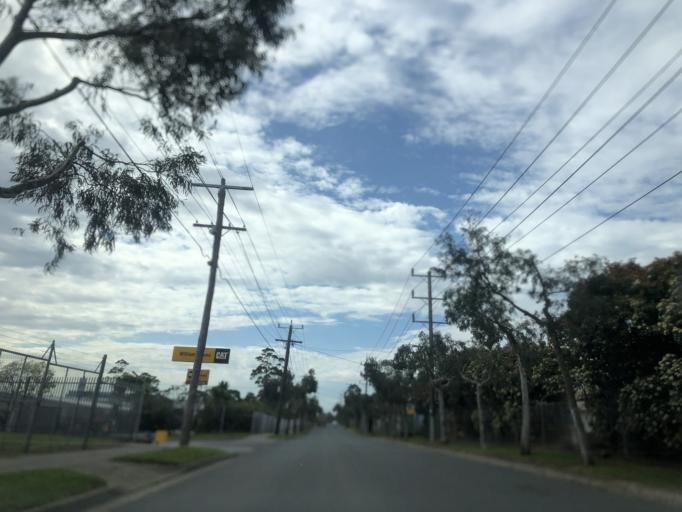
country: AU
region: Victoria
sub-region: Monash
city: Notting Hill
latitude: -37.9133
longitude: 145.1500
